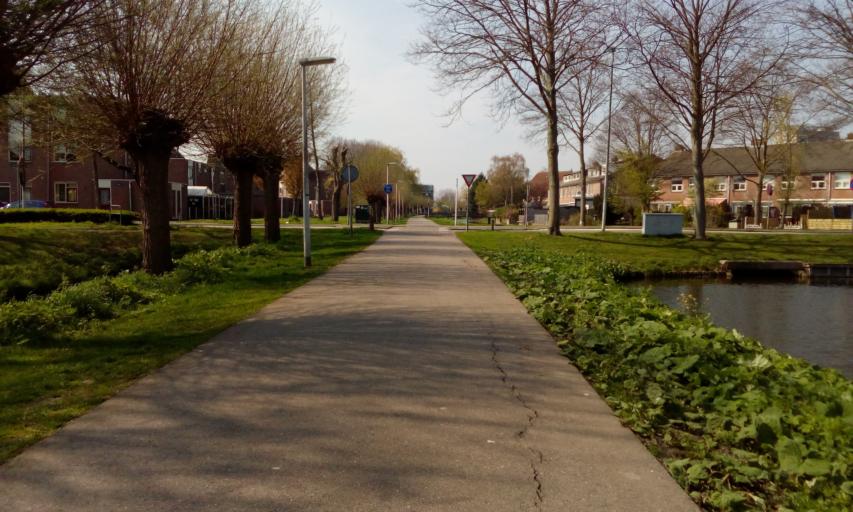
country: NL
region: South Holland
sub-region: Gemeente Spijkenisse
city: Spijkenisse
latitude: 51.8307
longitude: 4.3256
